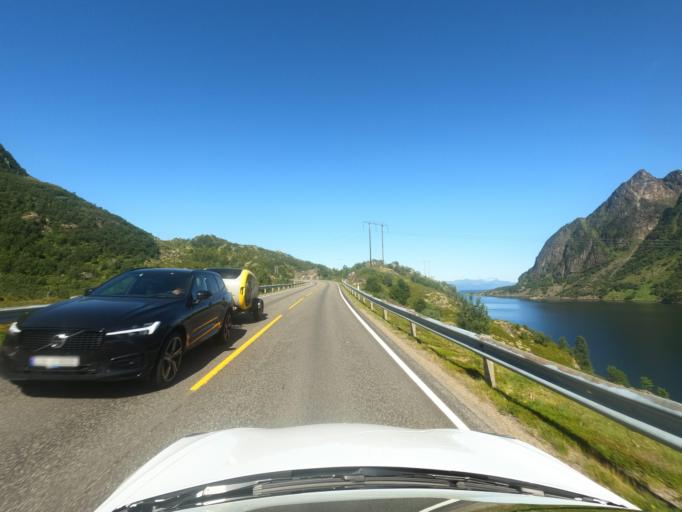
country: NO
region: Nordland
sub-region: Hadsel
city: Stokmarknes
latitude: 68.4360
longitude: 14.9871
